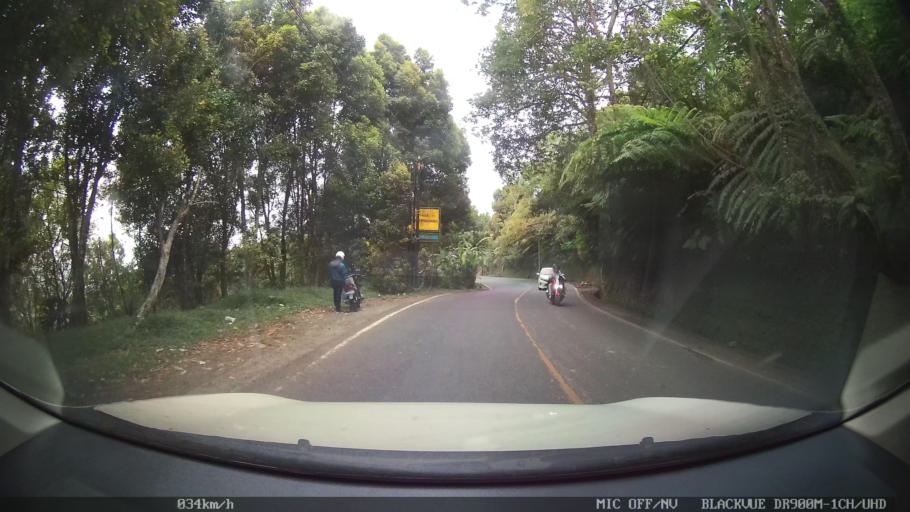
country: ID
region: Bali
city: Banjar Ambengan
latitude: -8.2157
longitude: 115.1428
